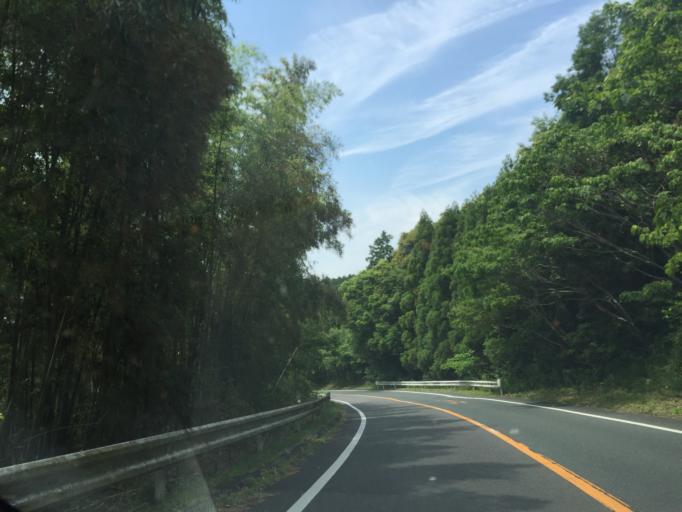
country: JP
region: Shizuoka
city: Kakegawa
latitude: 34.7971
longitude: 137.9957
